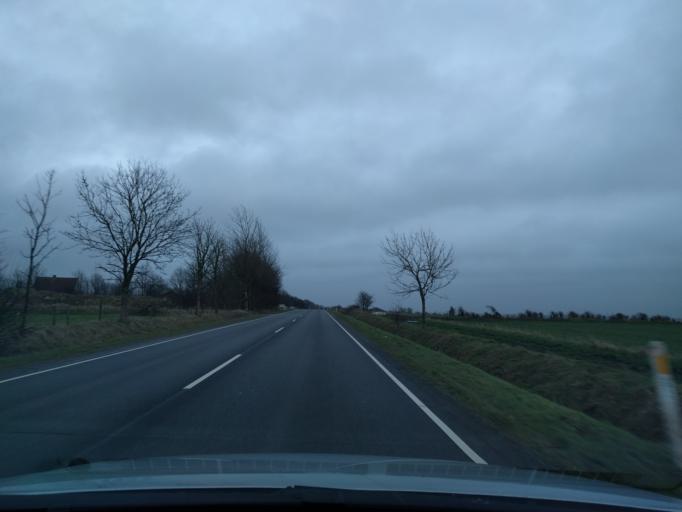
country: DK
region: South Denmark
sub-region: Tonder Kommune
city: Toftlund
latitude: 55.2526
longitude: 9.1552
